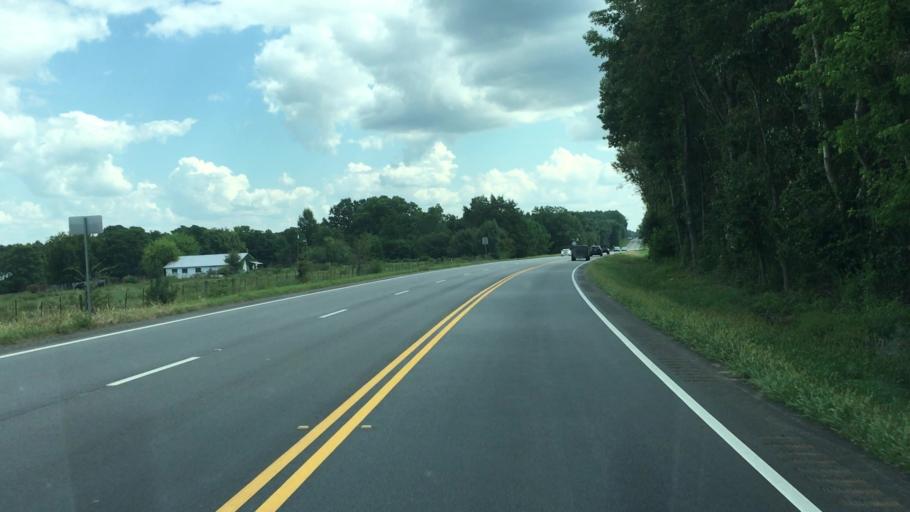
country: US
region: Georgia
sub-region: Putnam County
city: Jefferson
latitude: 33.4682
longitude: -83.4162
